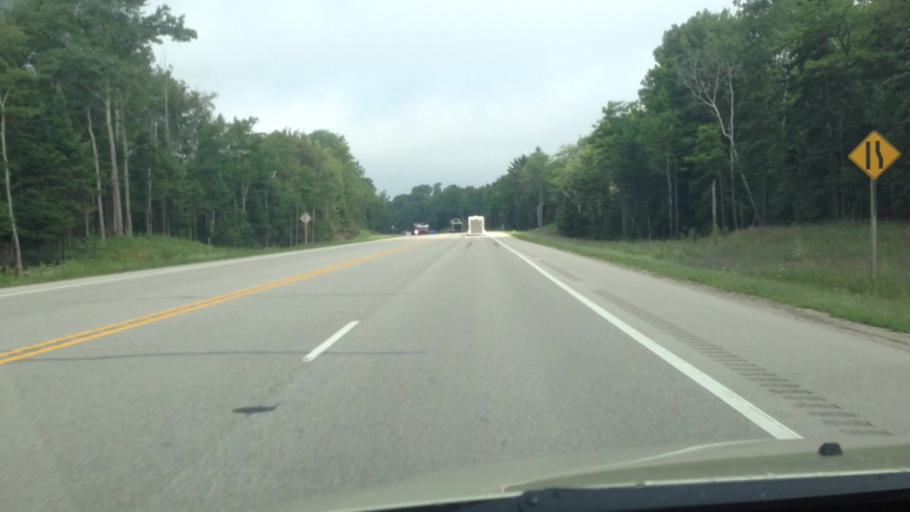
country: US
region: Michigan
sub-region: Luce County
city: Newberry
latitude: 46.0678
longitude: -85.1940
